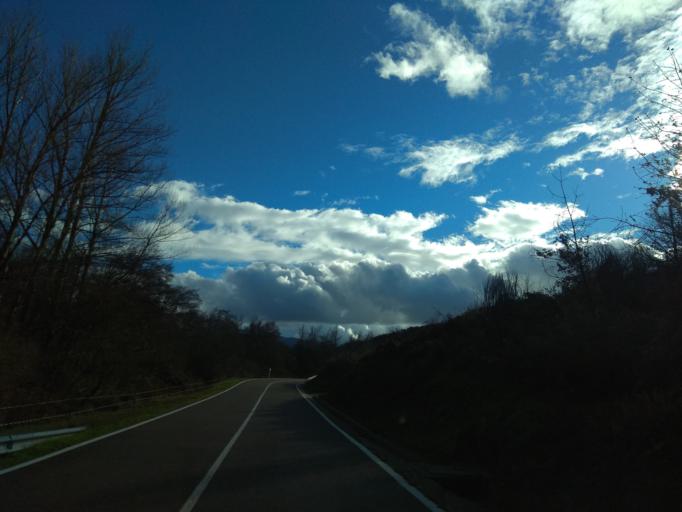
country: ES
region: Cantabria
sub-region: Provincia de Cantabria
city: San Martin de Elines
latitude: 42.8566
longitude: -3.9137
